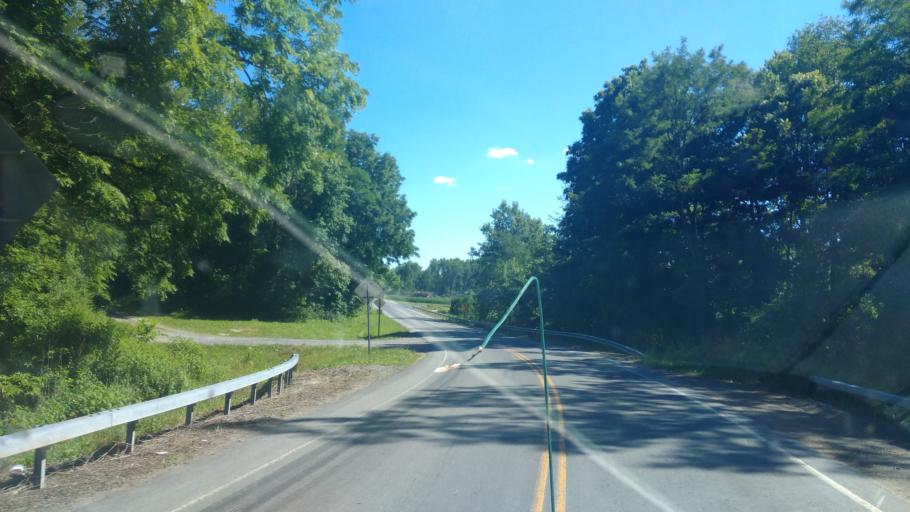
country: US
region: New York
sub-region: Wayne County
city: Lyons
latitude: 43.0314
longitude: -76.9540
